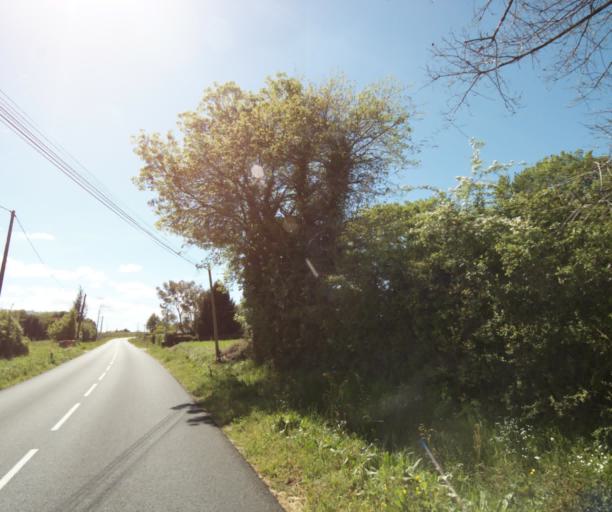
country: FR
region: Poitou-Charentes
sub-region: Departement de la Charente-Maritime
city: Fontcouverte
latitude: 45.7528
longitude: -0.5716
